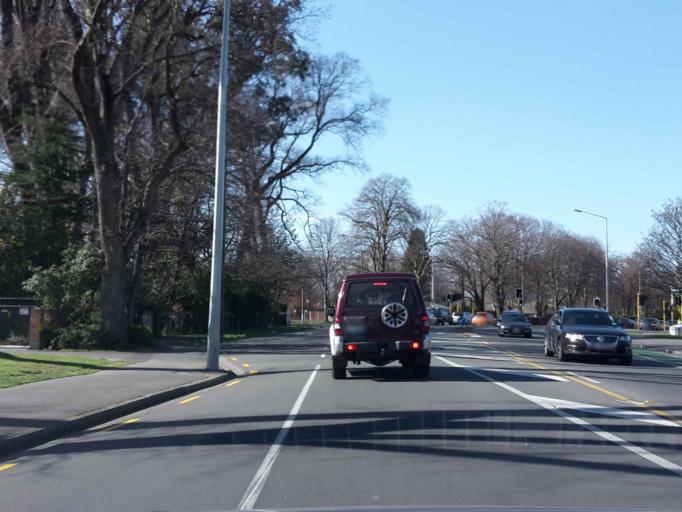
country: NZ
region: Canterbury
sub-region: Christchurch City
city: Christchurch
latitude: -43.5328
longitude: 172.5661
